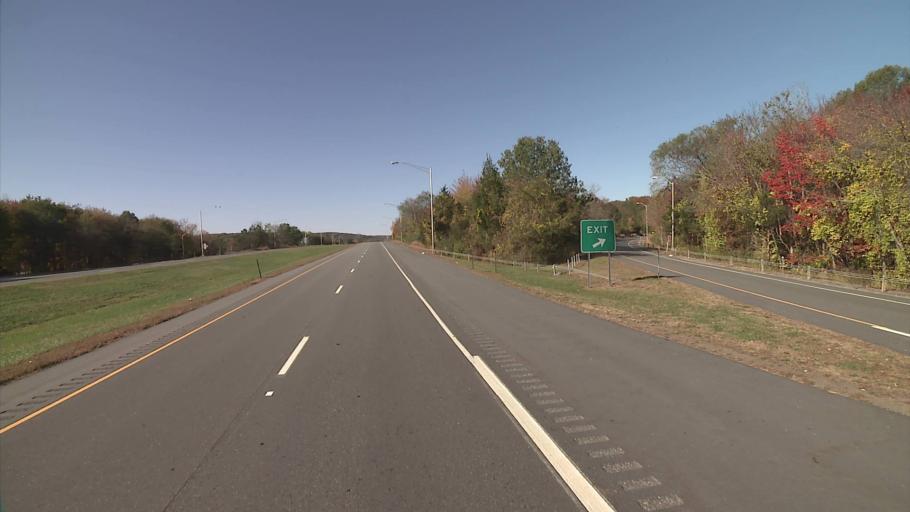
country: US
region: Connecticut
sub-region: Windham County
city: Willimantic
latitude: 41.7276
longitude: -72.2382
